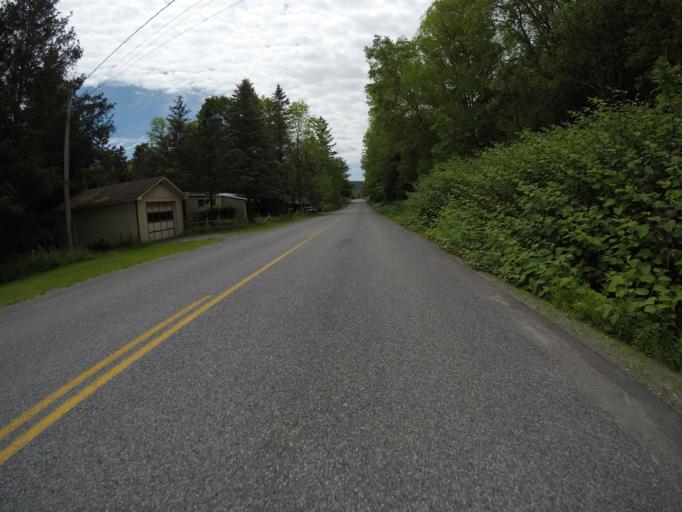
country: US
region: New York
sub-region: Delaware County
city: Stamford
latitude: 42.1995
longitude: -74.5775
